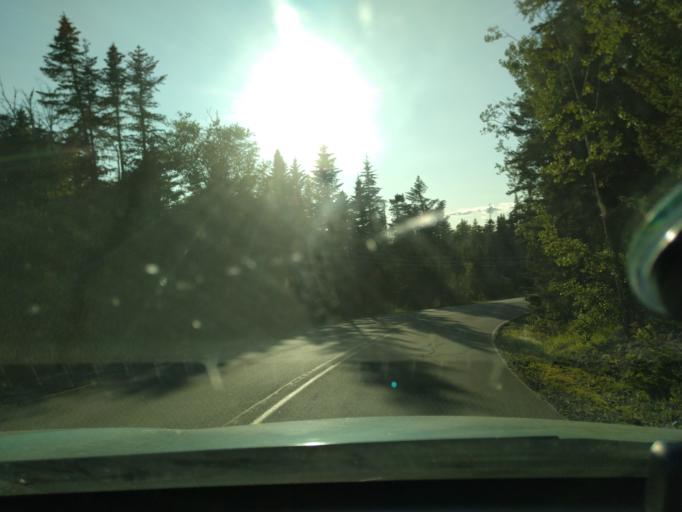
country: US
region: Maine
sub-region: Washington County
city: Machiasport
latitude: 44.6594
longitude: -67.2221
